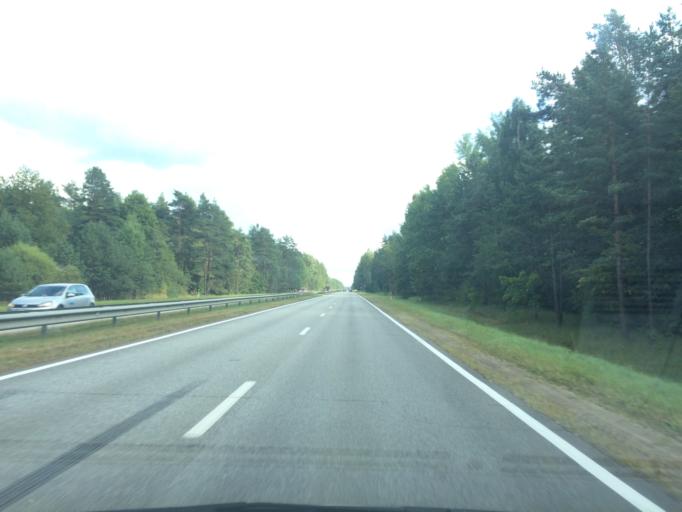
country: LV
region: Ikskile
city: Ikskile
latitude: 56.8337
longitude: 24.5055
